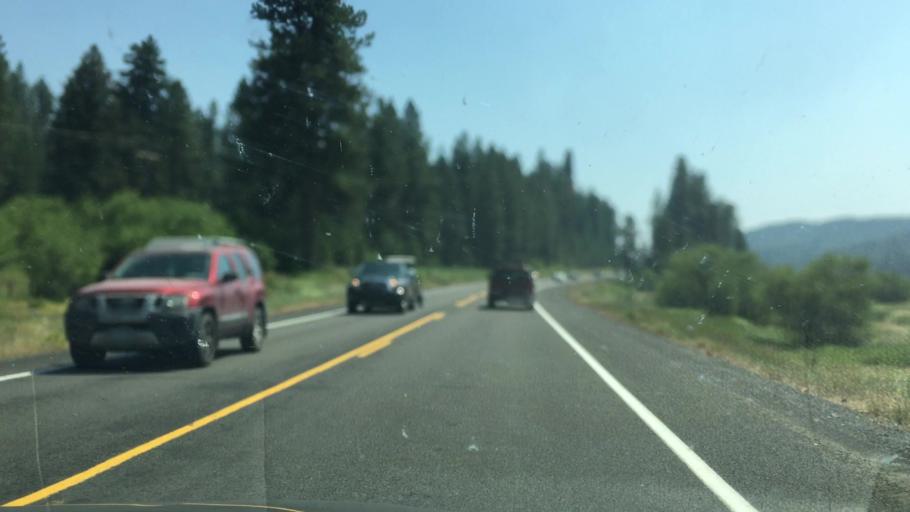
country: US
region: Idaho
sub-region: Valley County
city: McCall
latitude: 45.0857
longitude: -116.3052
